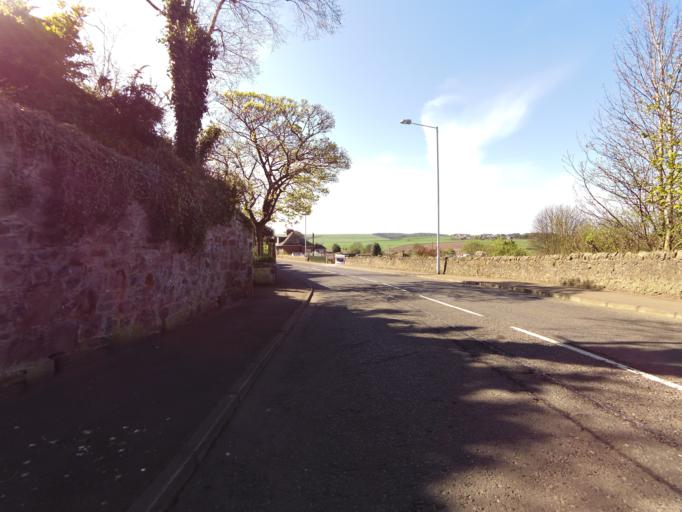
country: GB
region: Scotland
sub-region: Dundee City
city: Dundee
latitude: 56.4227
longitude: -2.9820
